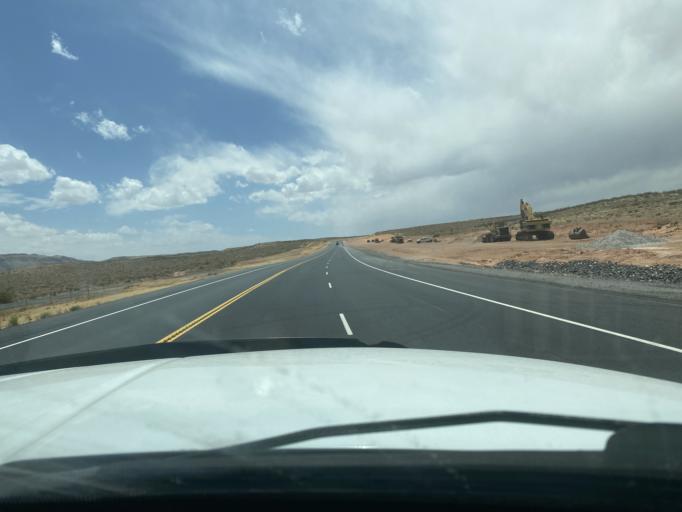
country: US
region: Utah
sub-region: Washington County
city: Hurricane
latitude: 37.1202
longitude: -113.3432
